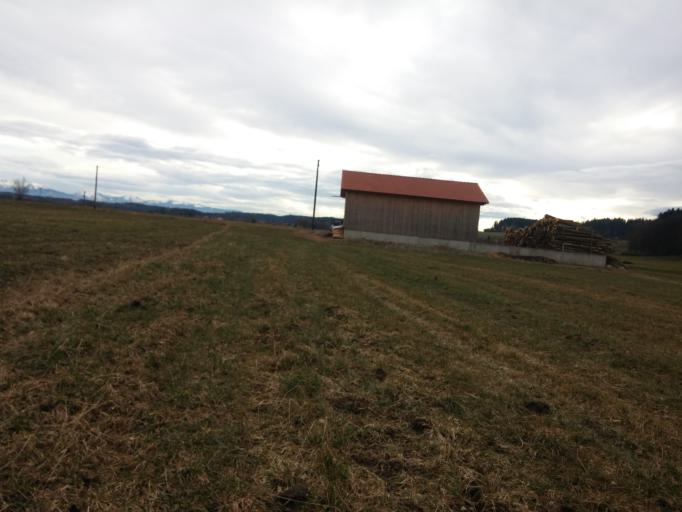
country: DE
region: Bavaria
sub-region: Upper Bavaria
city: Glonn
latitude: 48.0018
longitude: 11.8631
